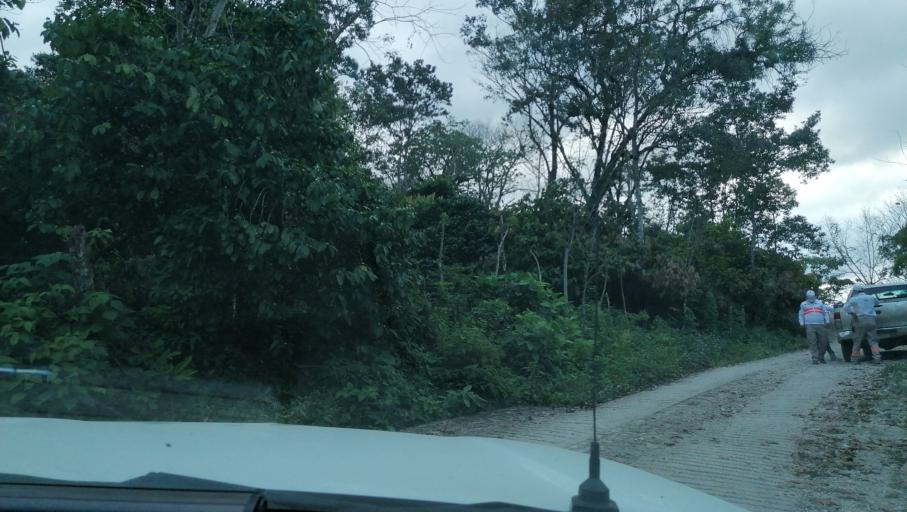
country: MX
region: Chiapas
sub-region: Francisco Leon
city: San Miguel la Sardina
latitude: 17.3104
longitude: -93.2666
